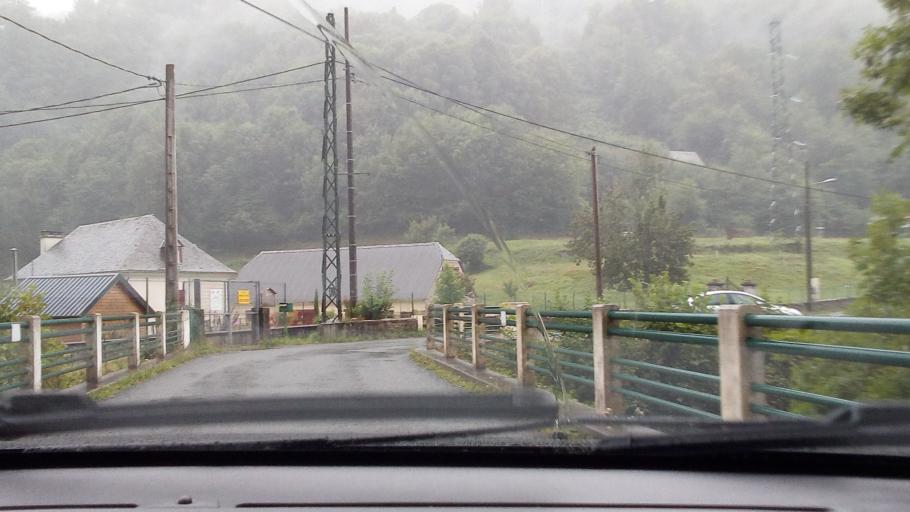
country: FR
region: Midi-Pyrenees
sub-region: Departement des Hautes-Pyrenees
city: Argeles-Gazost
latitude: 42.9826
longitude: -0.1435
